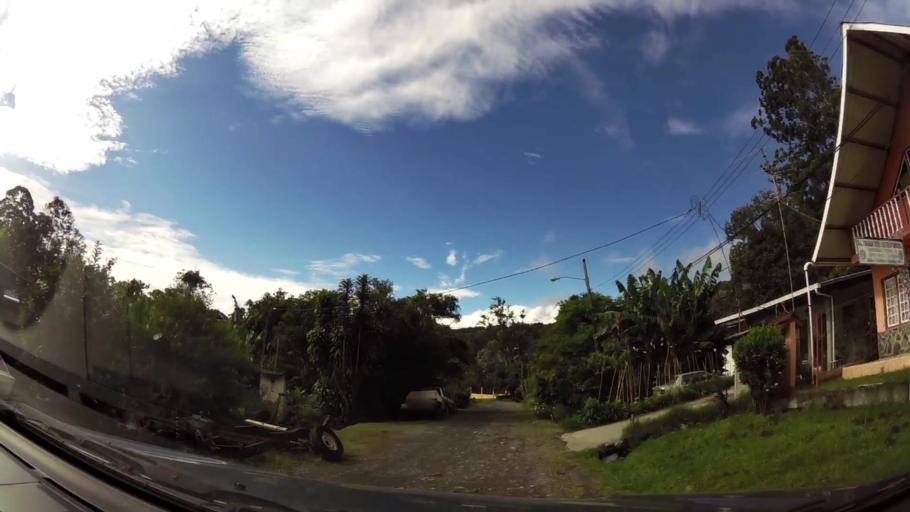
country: PA
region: Chiriqui
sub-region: Distrito Boquete
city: Boquete
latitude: 8.7800
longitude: -82.4343
